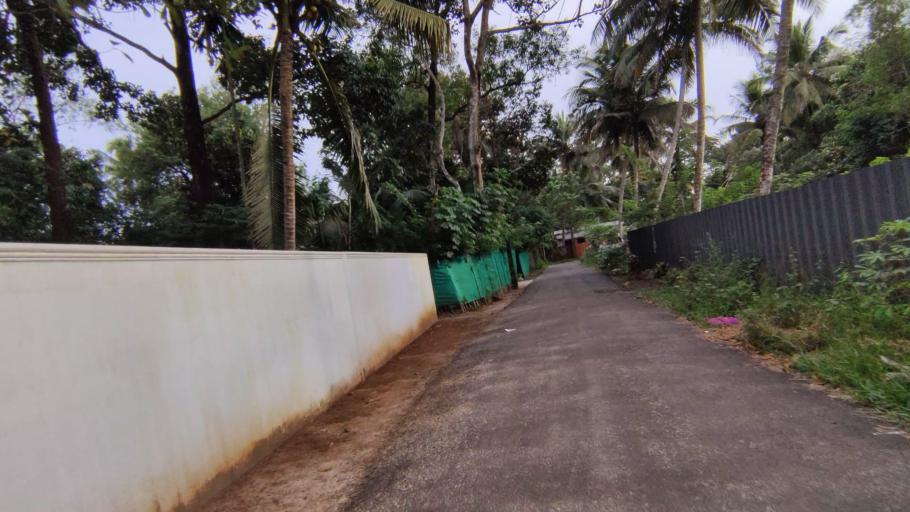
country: IN
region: Kerala
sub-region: Alappuzha
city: Shertallai
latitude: 9.6097
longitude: 76.3496
